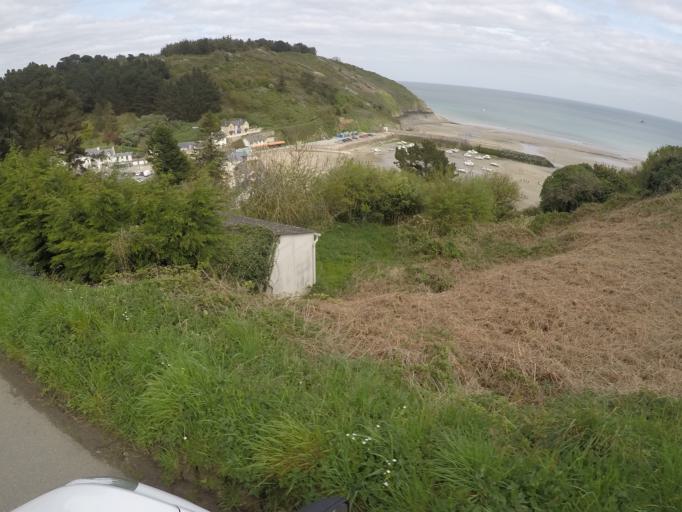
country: FR
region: Brittany
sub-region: Departement des Cotes-d'Armor
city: Plouezec
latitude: 48.7257
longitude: -2.9497
